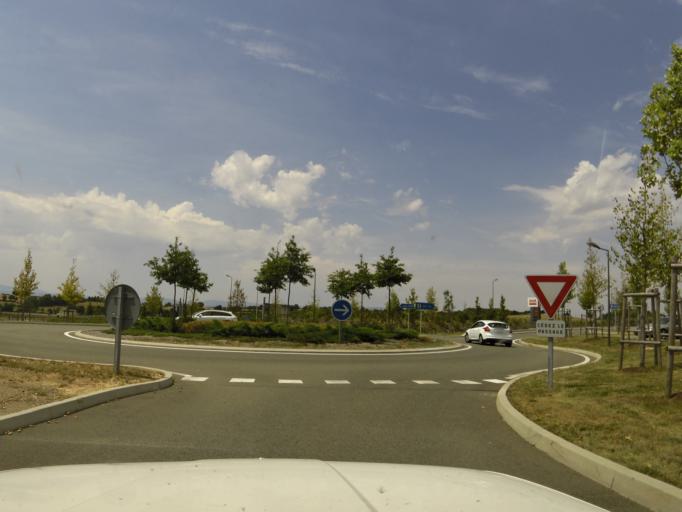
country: FR
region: Rhone-Alpes
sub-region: Departement de la Loire
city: Bussieres
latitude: 45.8499
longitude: 4.2255
